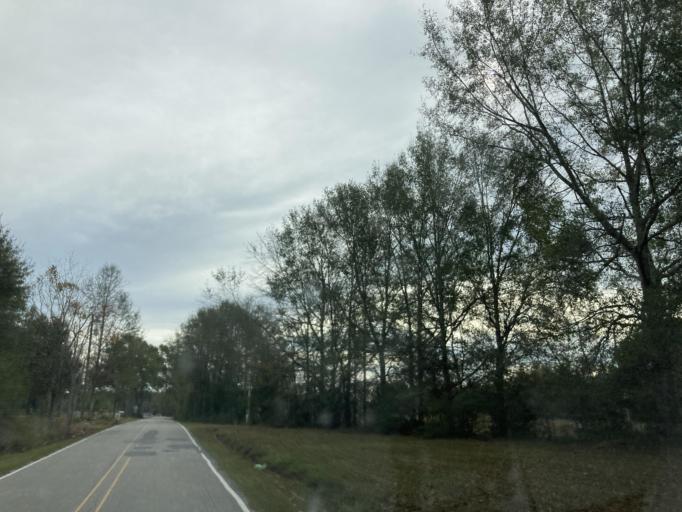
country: US
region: Mississippi
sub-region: Lamar County
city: Purvis
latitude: 31.1121
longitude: -89.4771
